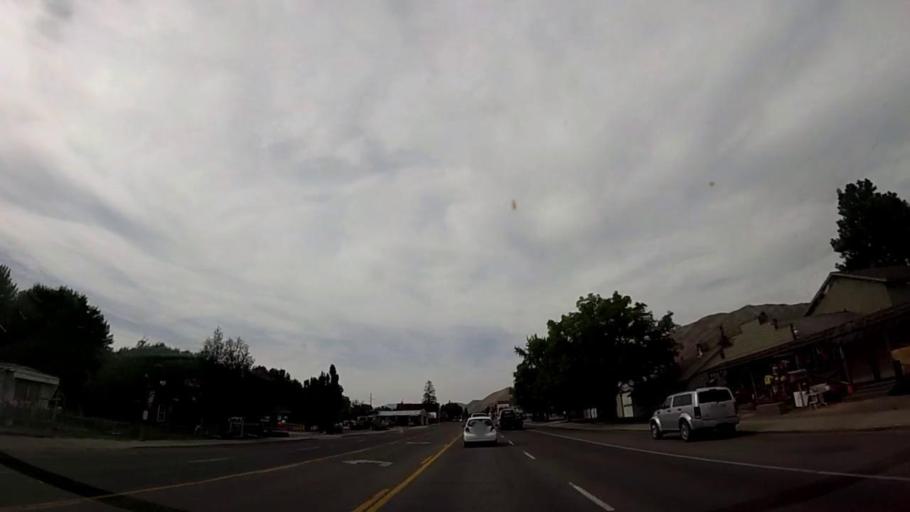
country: US
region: Idaho
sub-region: Blaine County
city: Bellevue
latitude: 43.4619
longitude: -114.2597
